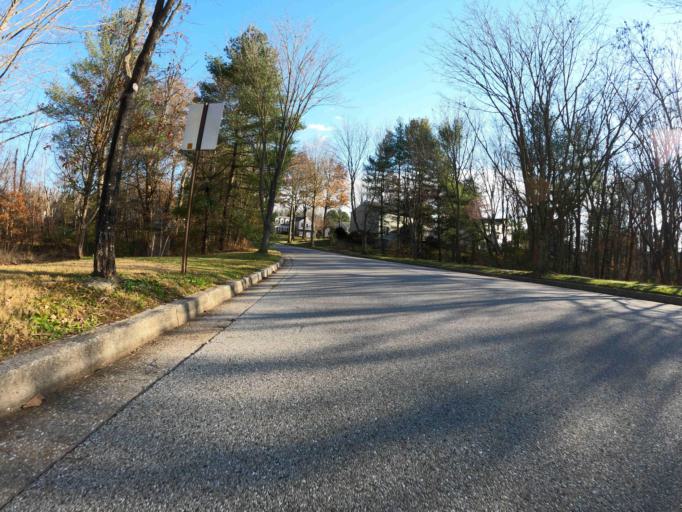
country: US
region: Maryland
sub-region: Howard County
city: Columbia
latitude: 39.2807
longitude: -76.8522
